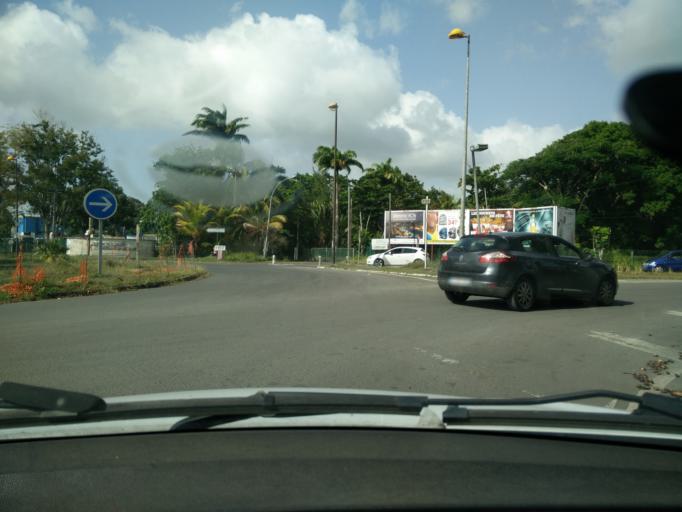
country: GP
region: Guadeloupe
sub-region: Guadeloupe
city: Pointe-a-Pitre
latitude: 16.2591
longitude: -61.5241
